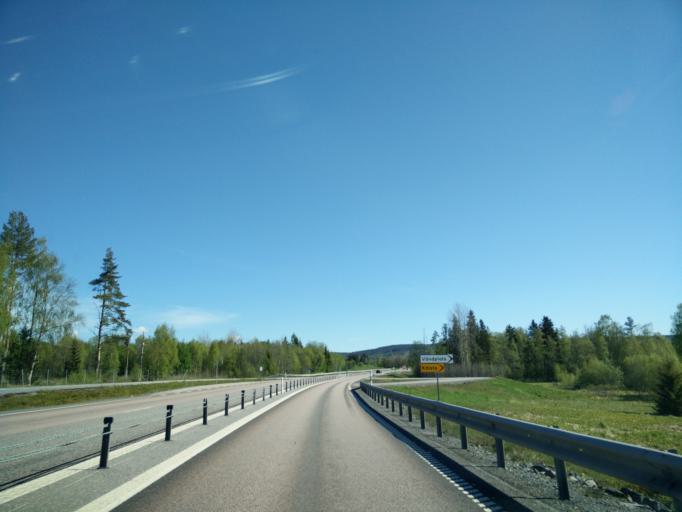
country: SE
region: Vaesternorrland
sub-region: Kramfors Kommun
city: Nordingra
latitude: 62.9955
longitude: 18.1652
